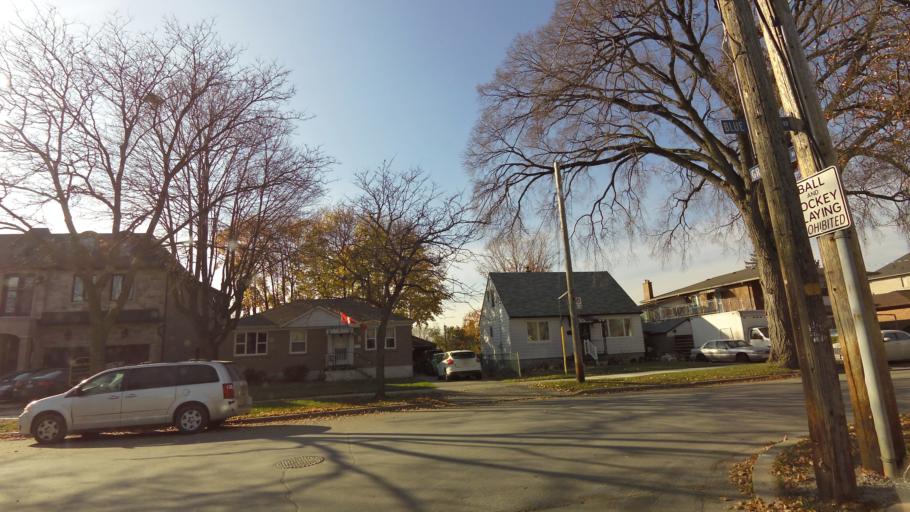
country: CA
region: Ontario
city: Toronto
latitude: 43.7166
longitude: -79.4899
